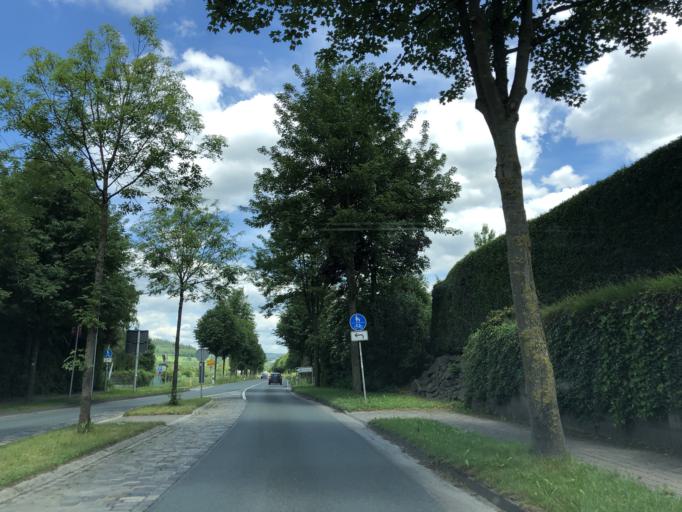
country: DE
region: North Rhine-Westphalia
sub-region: Regierungsbezirk Arnsberg
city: Schmallenberg
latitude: 51.1363
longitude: 8.2624
